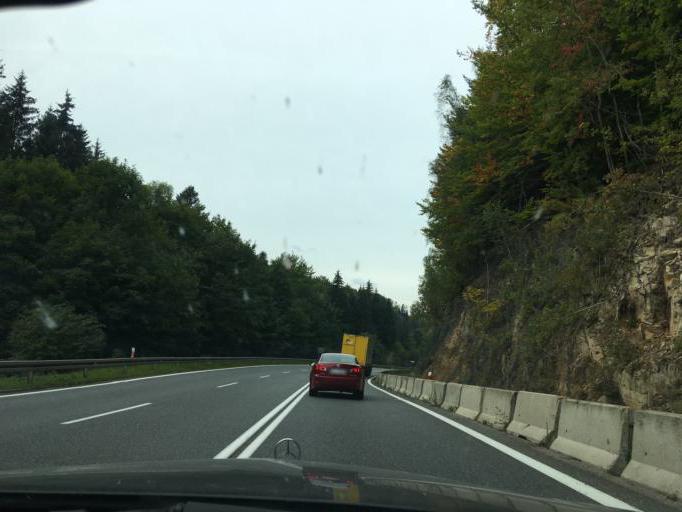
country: PL
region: Lower Silesian Voivodeship
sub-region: Powiat klodzki
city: Lewin Klodzki
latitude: 50.4007
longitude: 16.3408
